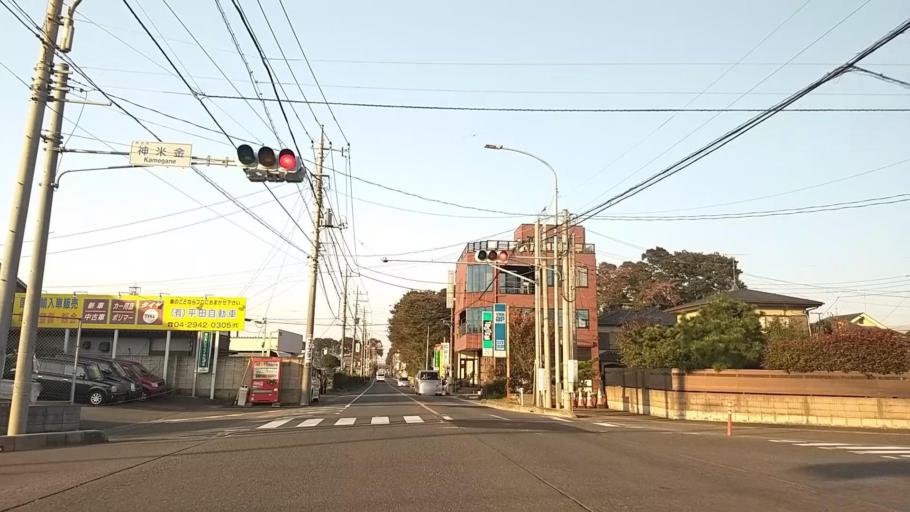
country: JP
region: Saitama
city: Tokorozawa
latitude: 35.8226
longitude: 139.4656
